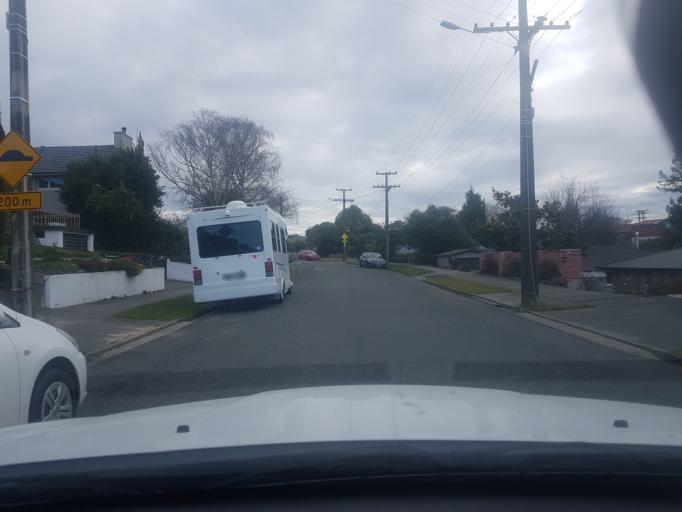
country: NZ
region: Canterbury
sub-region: Timaru District
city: Timaru
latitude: -44.3904
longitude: 171.2152
